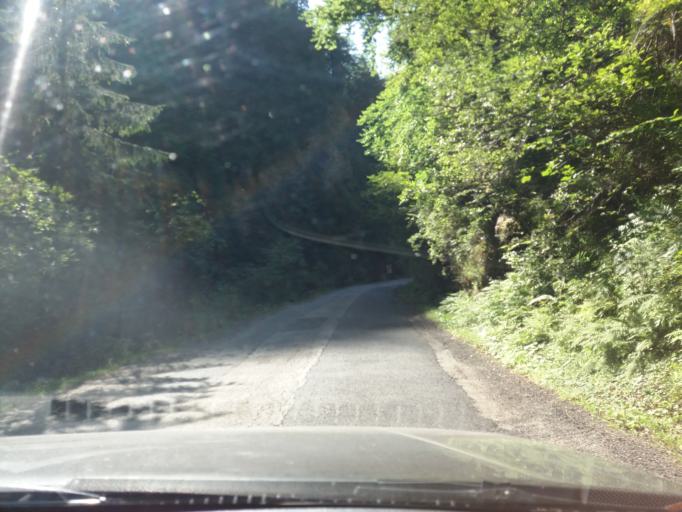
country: RO
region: Hunedoara
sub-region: Oras Petrila
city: Petrila
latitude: 45.4138
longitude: 23.4725
